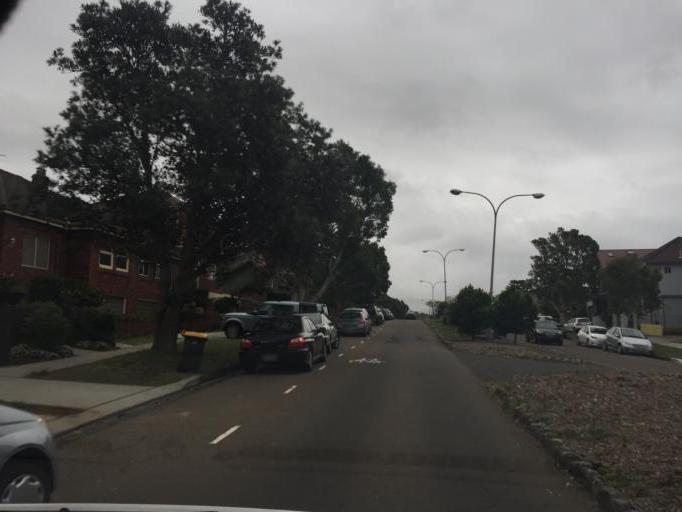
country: AU
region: New South Wales
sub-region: Waverley
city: North Bondi
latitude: -33.8857
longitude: 151.2791
